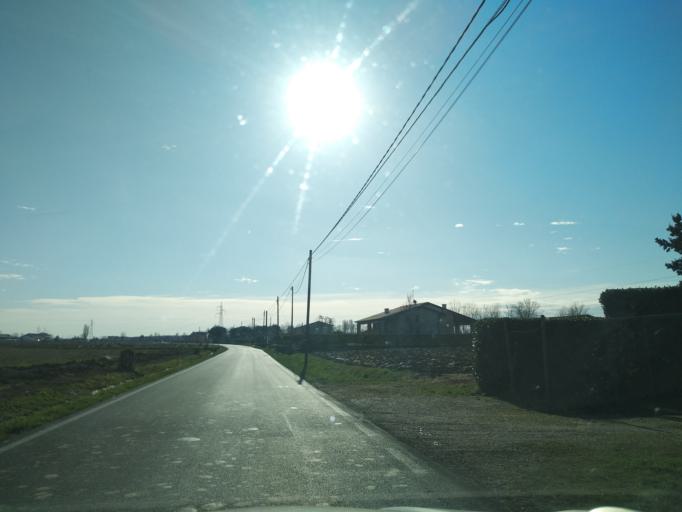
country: IT
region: Veneto
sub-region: Provincia di Padova
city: Bosco
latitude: 45.4535
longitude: 11.7936
